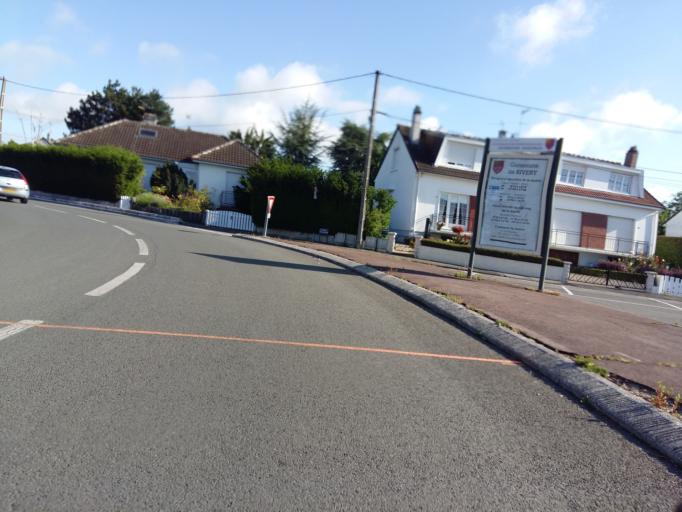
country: FR
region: Picardie
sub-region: Departement de la Somme
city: Rivery
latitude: 49.9056
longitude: 2.3269
